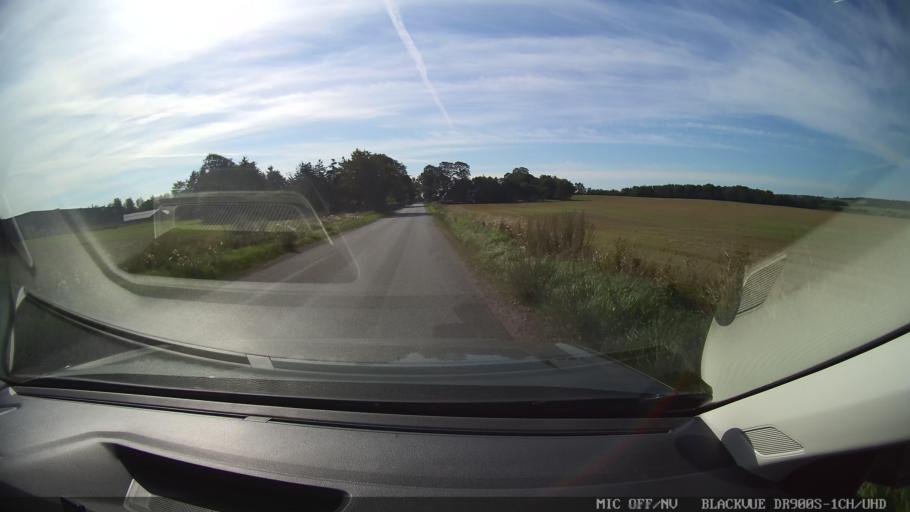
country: DK
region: North Denmark
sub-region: Mariagerfjord Kommune
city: Hobro
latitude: 56.5532
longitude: 9.8431
